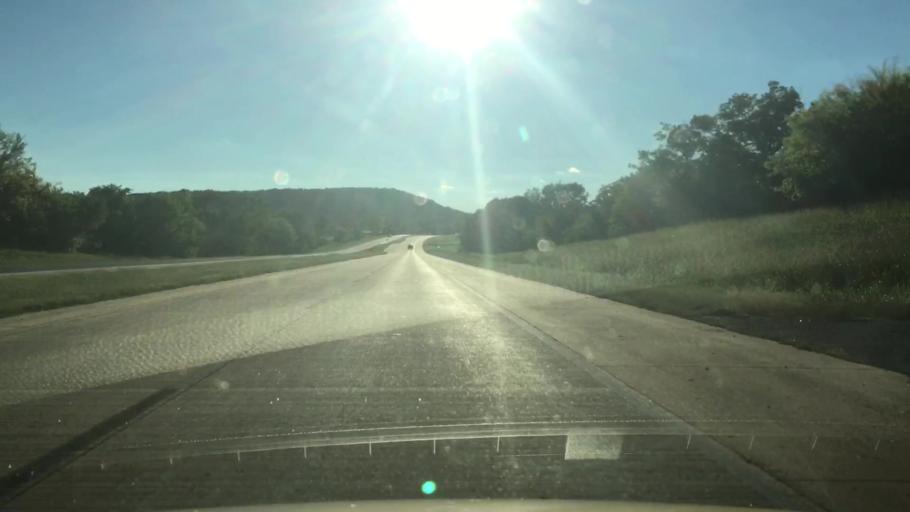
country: US
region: Oklahoma
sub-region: Cherokee County
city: Park Hill
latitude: 35.8047
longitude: -95.0821
